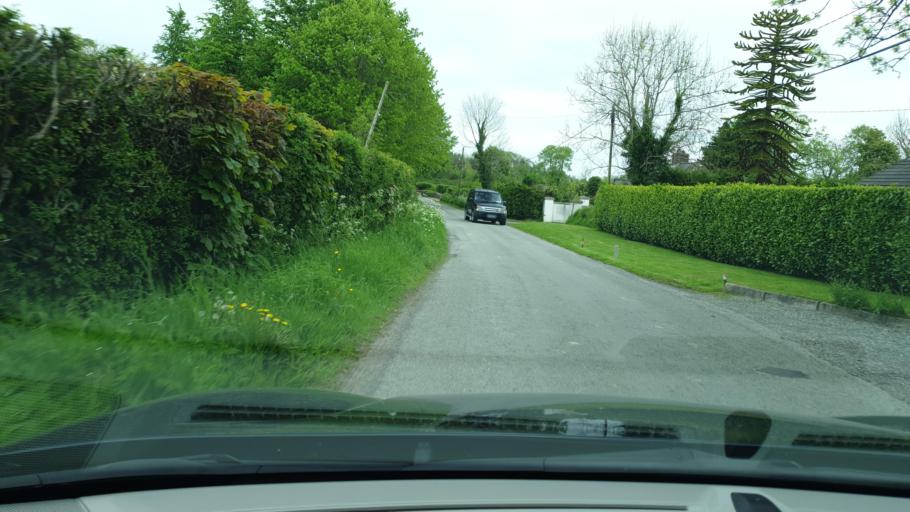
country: IE
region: Leinster
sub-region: An Mhi
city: Dunboyne
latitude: 53.4425
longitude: -6.5226
